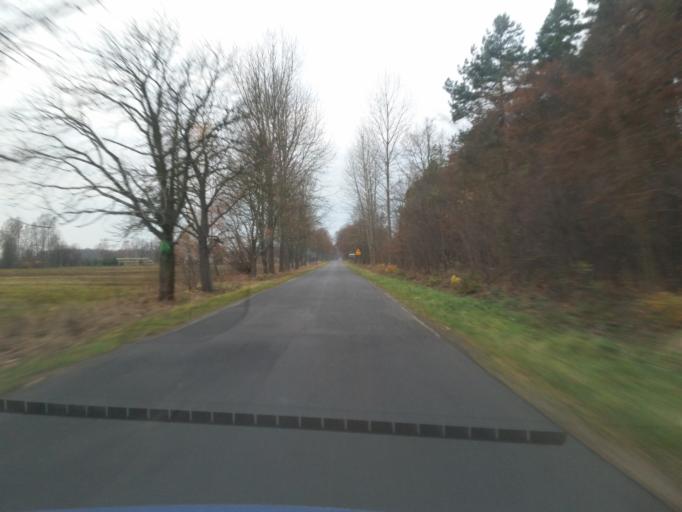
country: PL
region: Silesian Voivodeship
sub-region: Powiat czestochowski
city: Borowno
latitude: 50.9661
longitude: 19.3022
